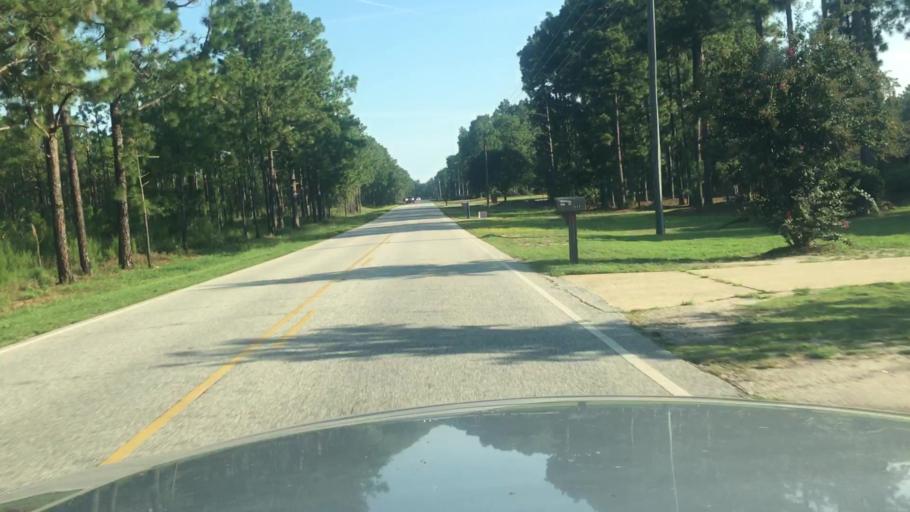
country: US
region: North Carolina
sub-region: Harnett County
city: Walkertown
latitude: 35.2164
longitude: -78.8650
